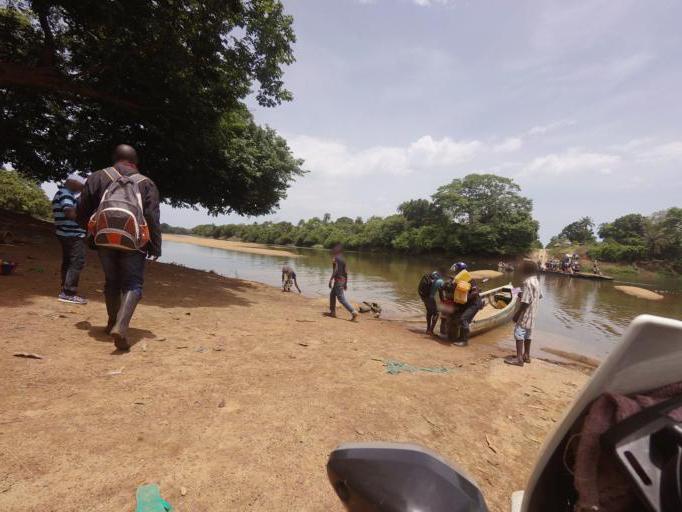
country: SL
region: Northern Province
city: Kamakwie
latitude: 9.4830
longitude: -12.3916
